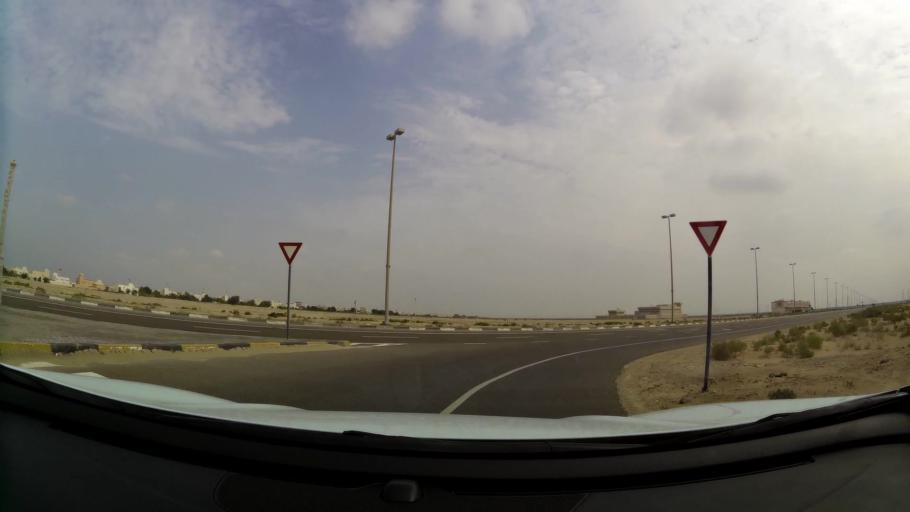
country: AE
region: Abu Dhabi
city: Abu Dhabi
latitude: 24.6379
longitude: 54.6719
